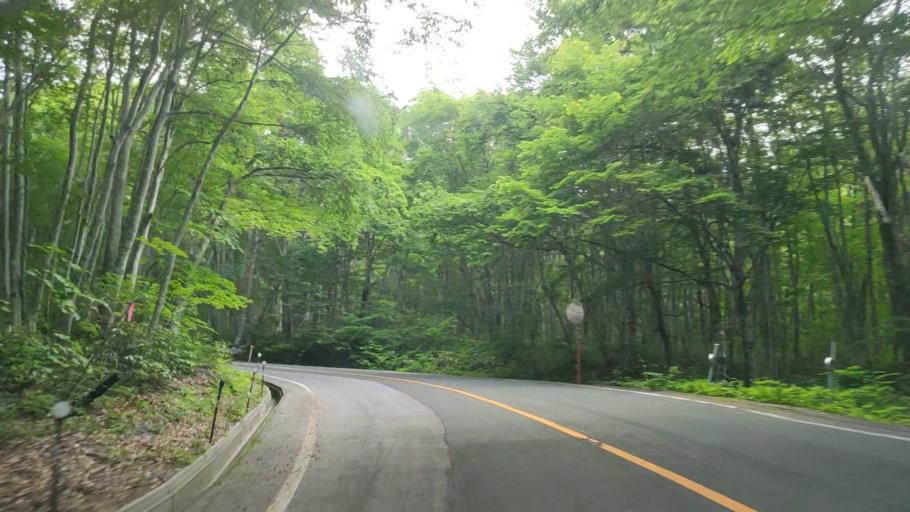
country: JP
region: Tottori
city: Yonago
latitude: 35.3460
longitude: 133.5547
